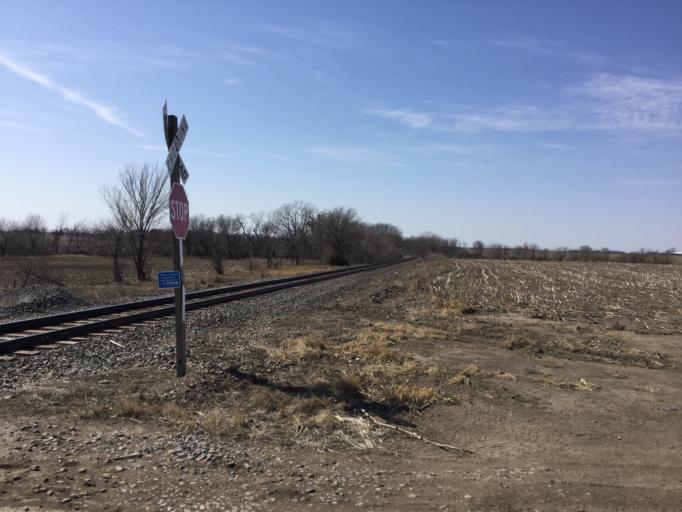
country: US
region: Kansas
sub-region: Marshall County
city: Marysville
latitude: 39.8452
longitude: -96.5013
